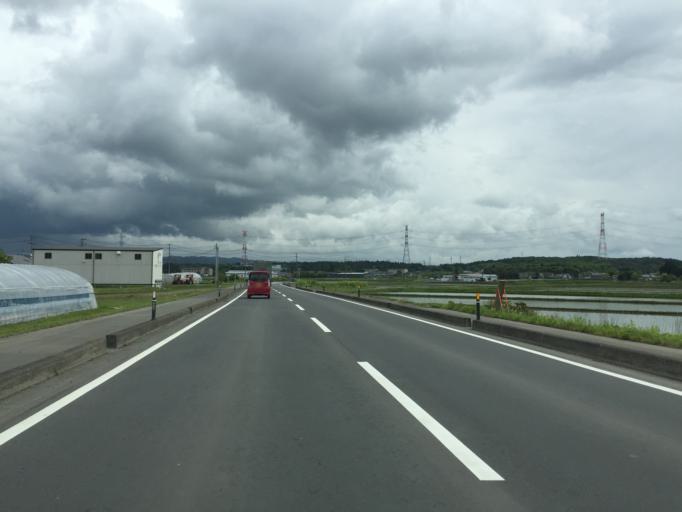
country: JP
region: Fukushima
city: Ishikawa
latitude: 37.0666
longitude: 140.3713
